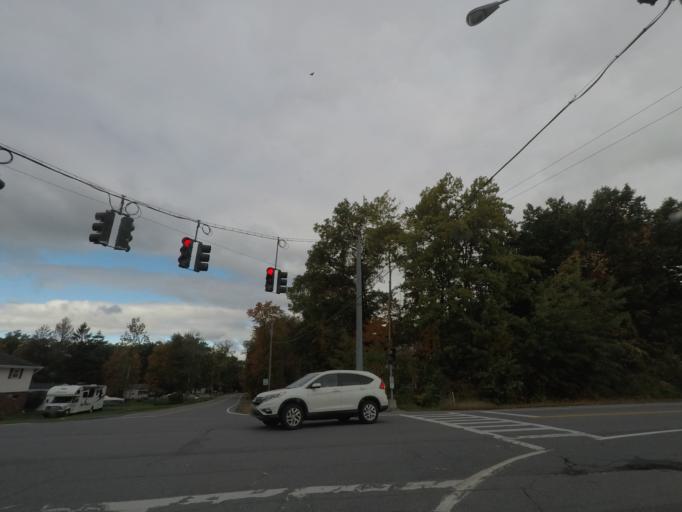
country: US
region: New York
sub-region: Saratoga County
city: Mechanicville
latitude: 42.8535
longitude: -73.7271
